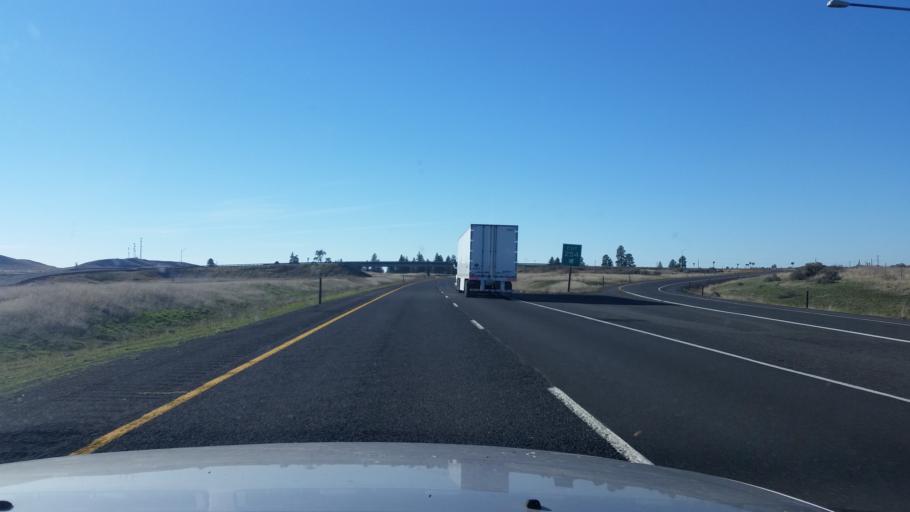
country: US
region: Washington
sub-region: Spokane County
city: Medical Lake
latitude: 47.3983
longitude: -117.8377
